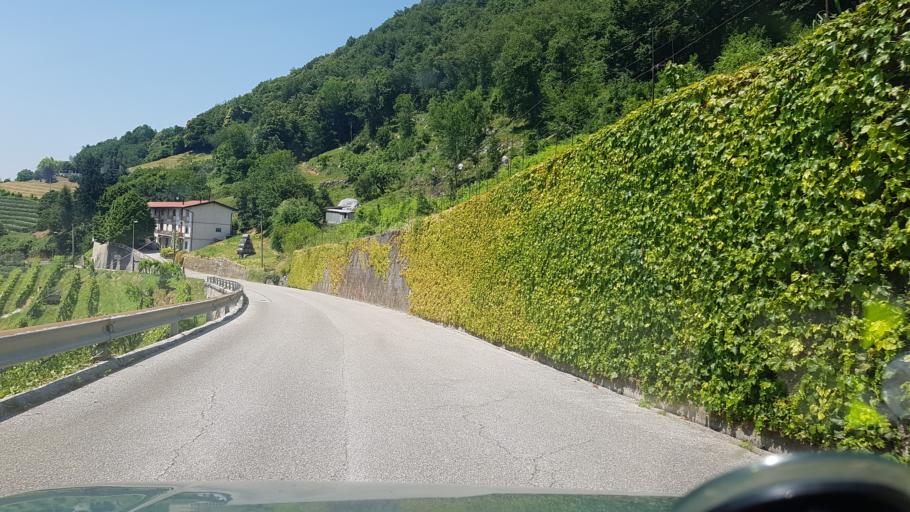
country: IT
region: Friuli Venezia Giulia
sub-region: Provincia di Udine
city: Nimis
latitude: 46.2219
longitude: 13.2589
